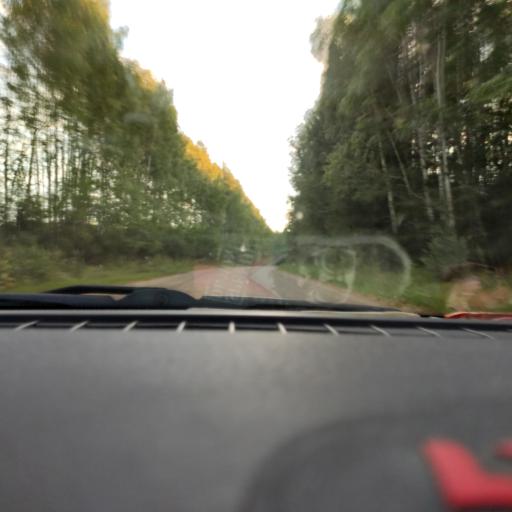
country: RU
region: Perm
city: Pavlovskiy
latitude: 57.9875
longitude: 54.8688
